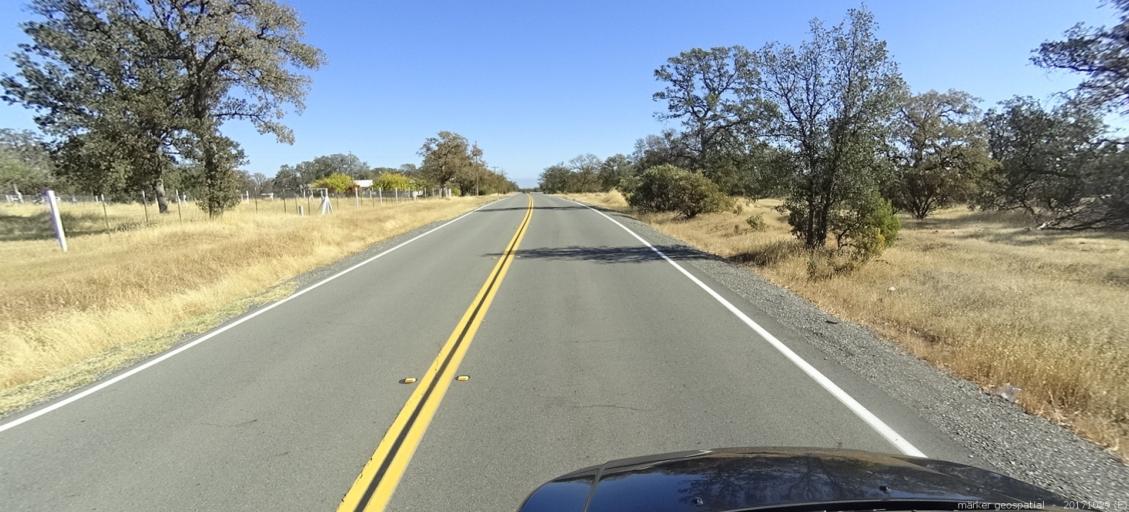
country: US
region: California
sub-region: Shasta County
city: Shasta
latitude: 40.4897
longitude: -122.5477
